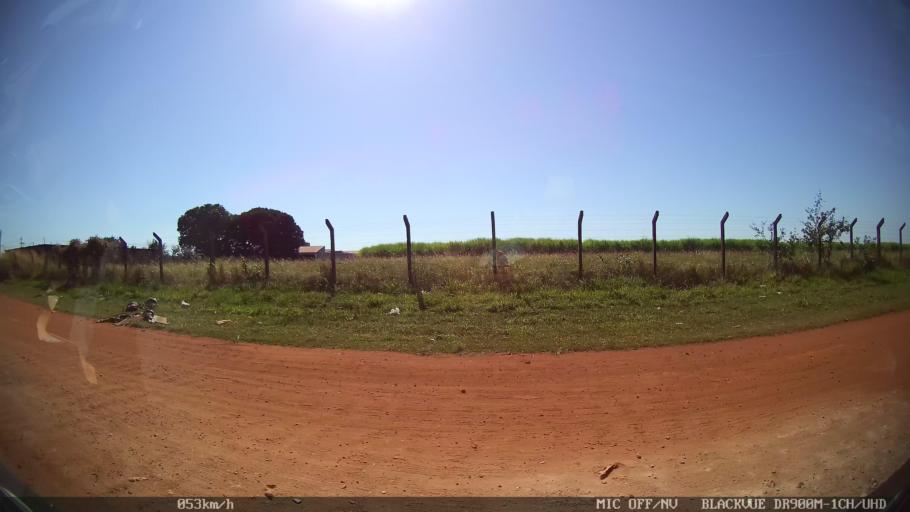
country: BR
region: Sao Paulo
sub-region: Batatais
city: Batatais
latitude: -20.8767
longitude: -47.5789
